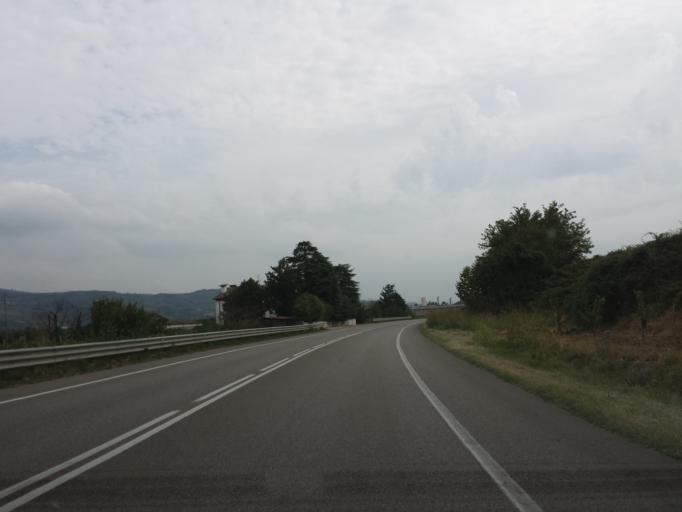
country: IT
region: Veneto
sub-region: Provincia di Verona
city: Brognoligo-Costalunga
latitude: 45.4635
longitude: 11.2891
